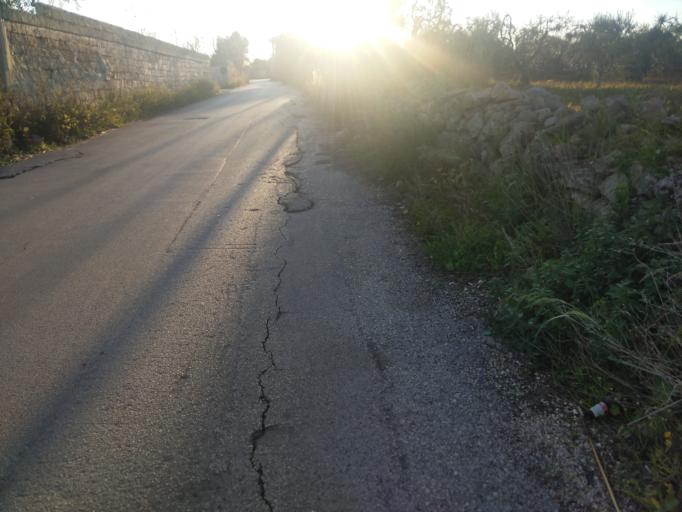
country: IT
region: Apulia
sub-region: Provincia di Bari
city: Bari
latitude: 41.1080
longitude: 16.8356
